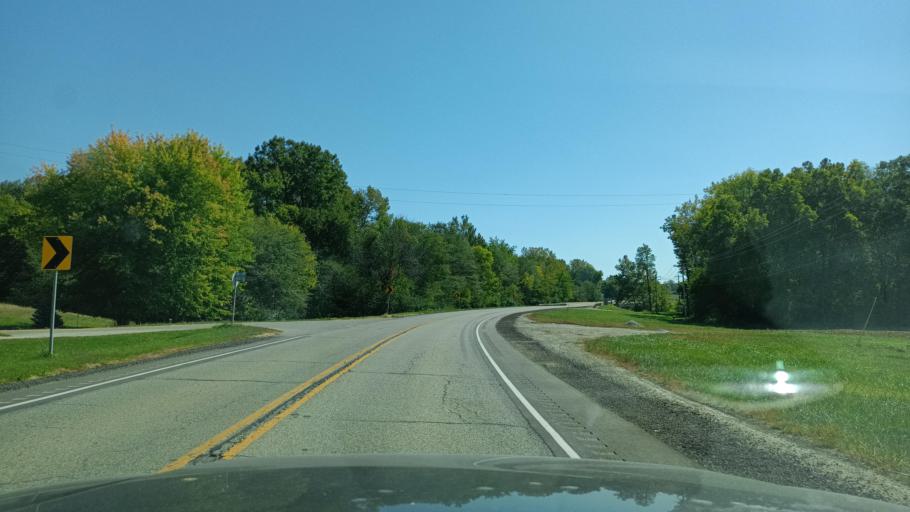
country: US
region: Illinois
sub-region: Woodford County
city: Eureka
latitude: 40.6254
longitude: -89.2436
